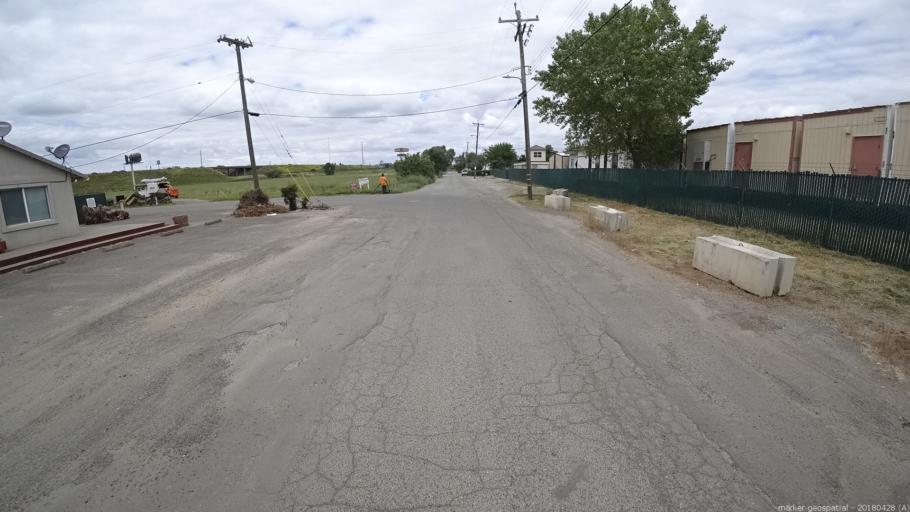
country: US
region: California
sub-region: Yolo County
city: West Sacramento
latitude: 38.5817
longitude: -121.5548
